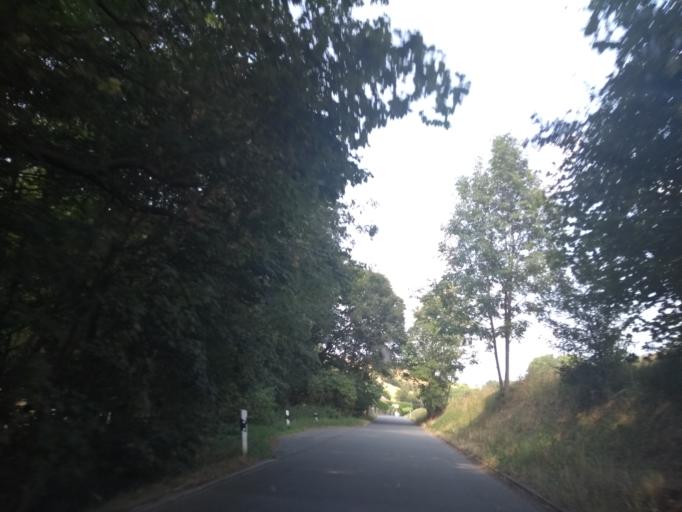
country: DE
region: Thuringia
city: Walpernhain
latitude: 51.0004
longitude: 11.9755
